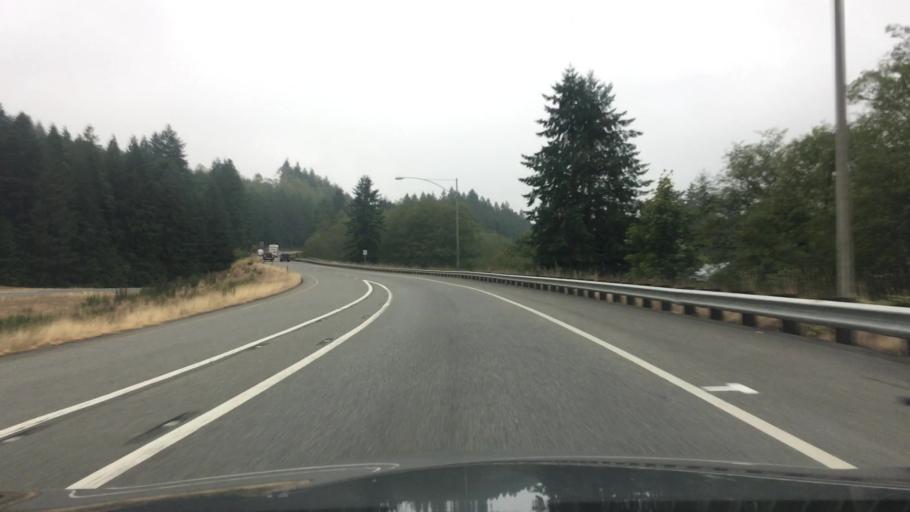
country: US
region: Washington
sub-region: Jefferson County
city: Port Hadlock-Irondale
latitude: 47.9540
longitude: -122.8841
